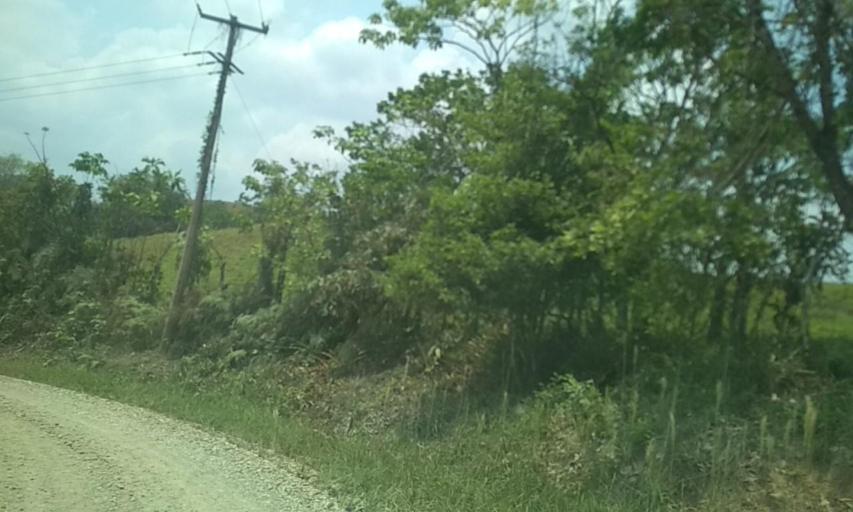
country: MX
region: Tabasco
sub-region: Huimanguillo
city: Francisco Rueda
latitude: 17.6193
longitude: -93.8145
